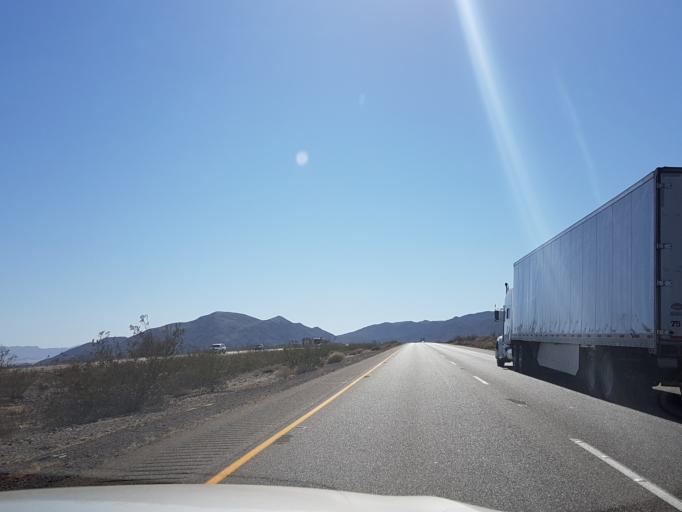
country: US
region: California
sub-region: San Bernardino County
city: Fort Irwin
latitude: 35.2178
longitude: -116.1109
